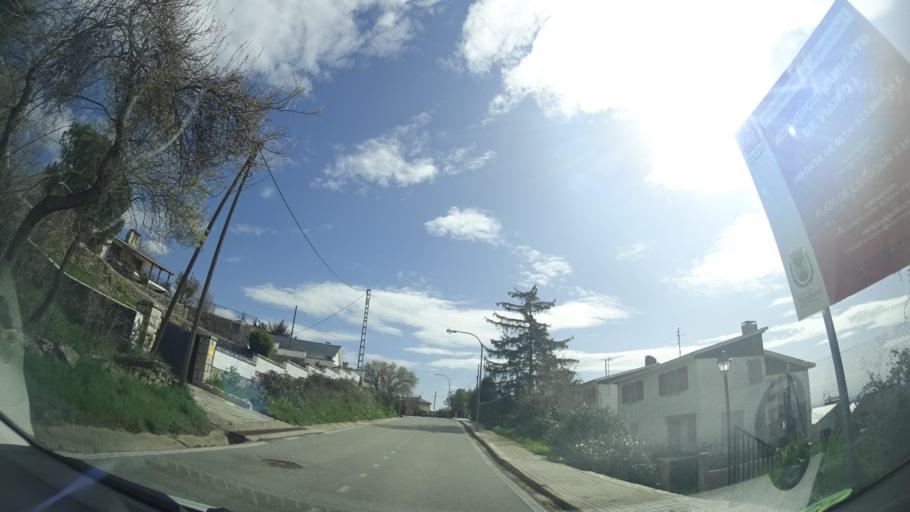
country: ES
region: Madrid
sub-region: Provincia de Madrid
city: Miraflores de la Sierra
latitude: 40.8161
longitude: -3.7656
